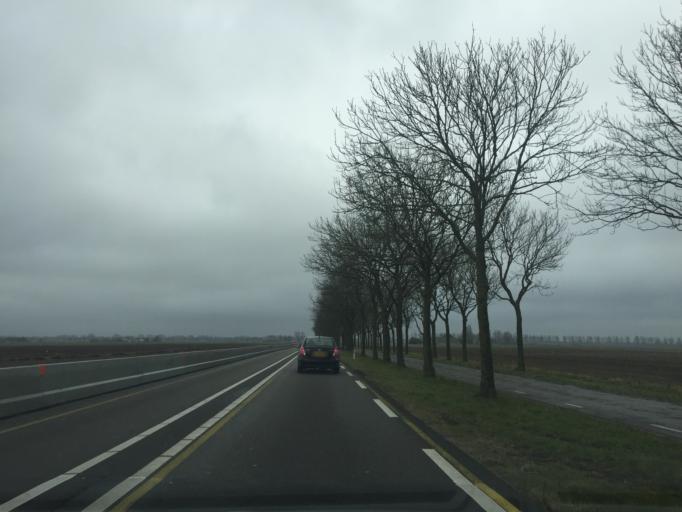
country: NL
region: South Holland
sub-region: Gemeente Kaag en Braassem
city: Oude Wetering
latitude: 52.1792
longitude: 4.6711
